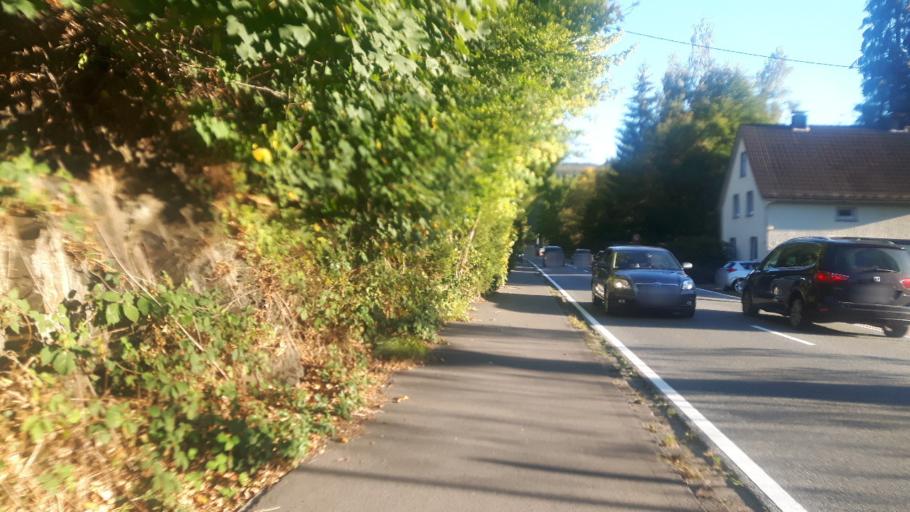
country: DE
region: Rheinland-Pfalz
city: Kirchen
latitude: 50.8200
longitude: 7.8900
